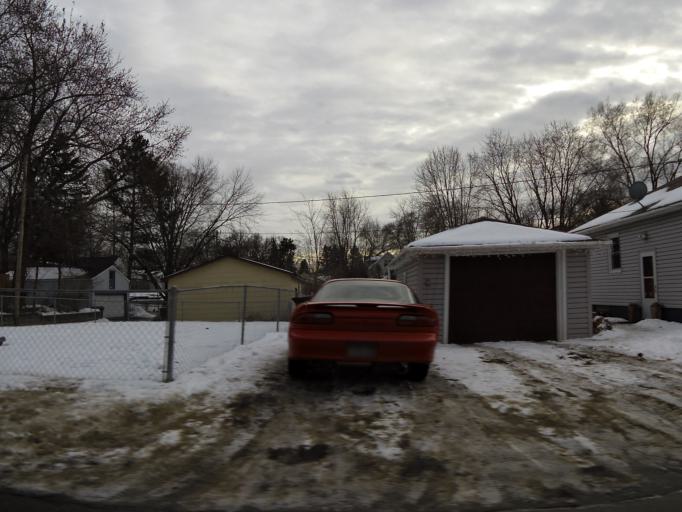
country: US
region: Minnesota
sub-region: Washington County
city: Oakdale
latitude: 44.9590
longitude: -92.9794
